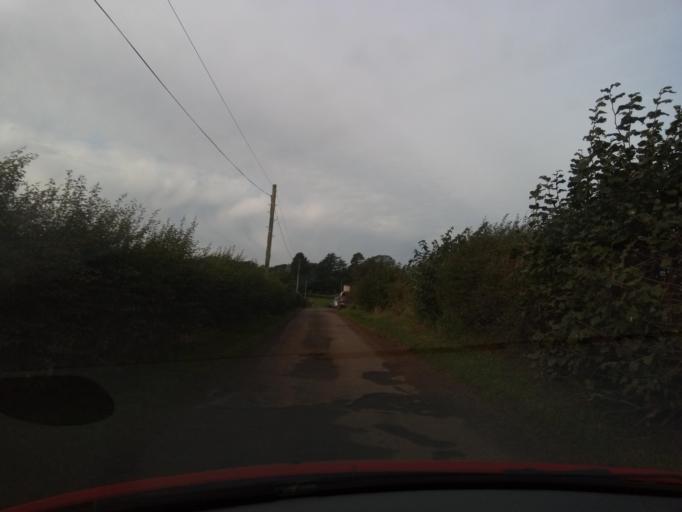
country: GB
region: Scotland
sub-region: The Scottish Borders
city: Kelso
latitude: 55.5793
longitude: -2.3631
